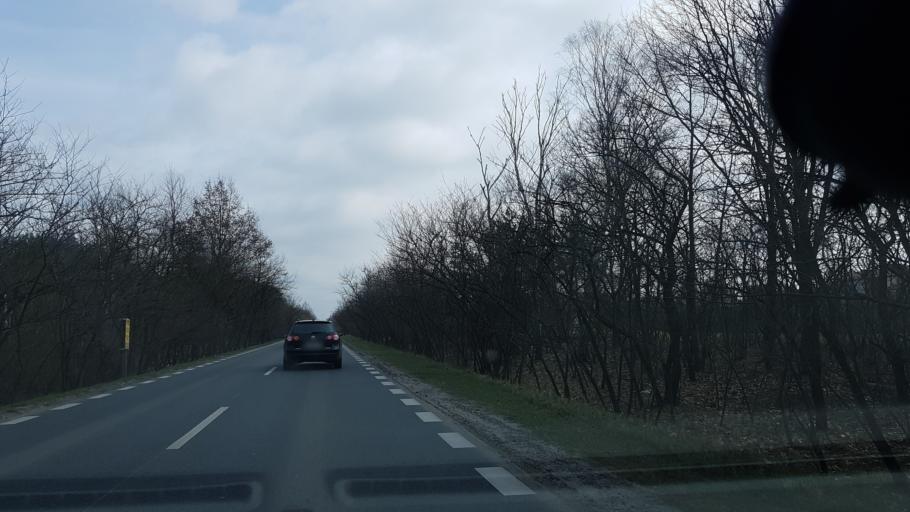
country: PL
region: Masovian Voivodeship
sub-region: Warszawa
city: Wesola
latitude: 52.2549
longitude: 21.2150
